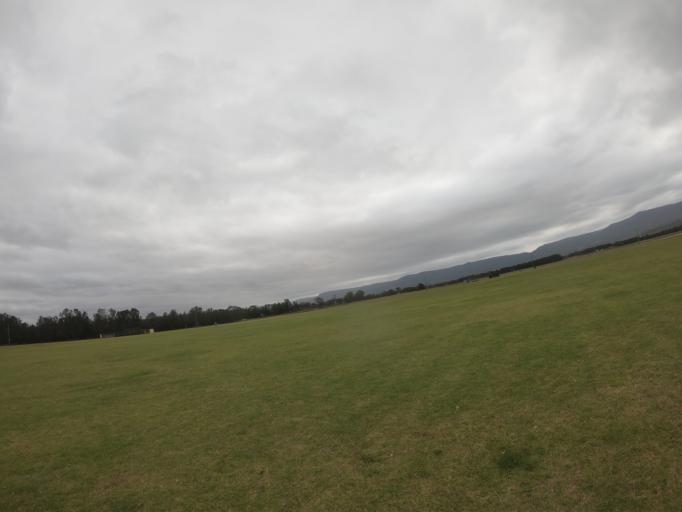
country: AU
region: New South Wales
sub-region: Wollongong
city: Berkeley
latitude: -34.4825
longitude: 150.8354
